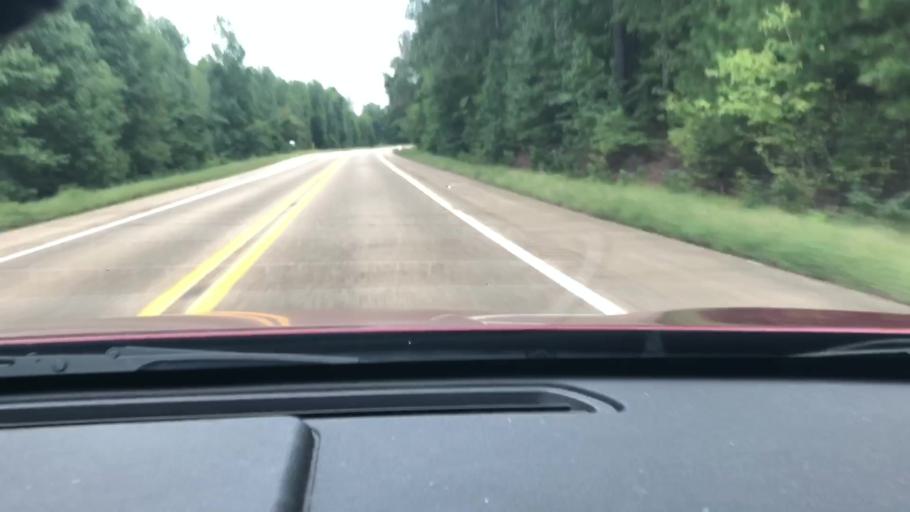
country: US
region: Arkansas
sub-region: Miller County
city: Texarkana
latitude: 33.4195
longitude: -93.8292
